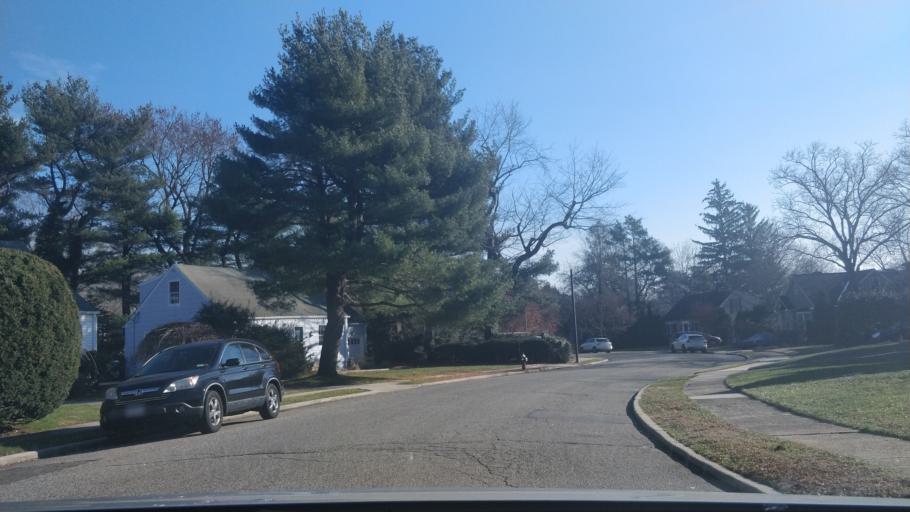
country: US
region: New York
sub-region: Nassau County
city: Locust Valley
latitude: 40.8802
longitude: -73.5825
